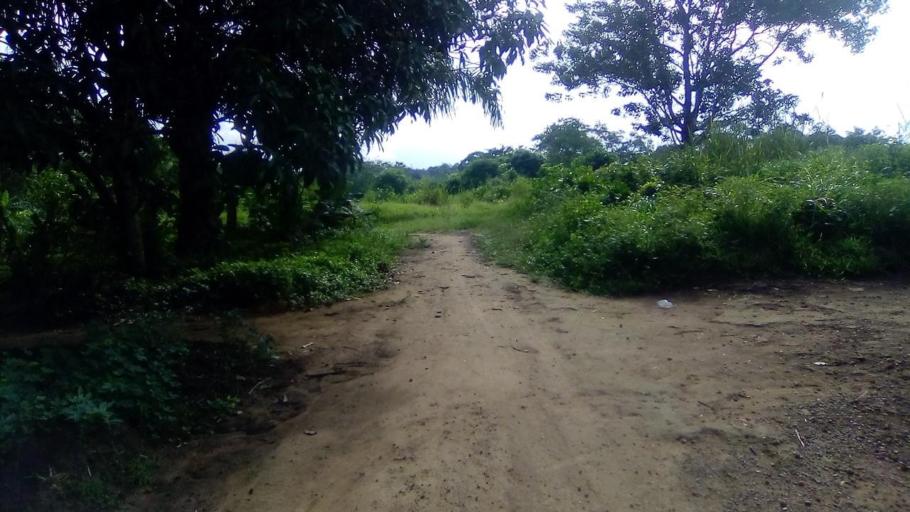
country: SL
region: Southern Province
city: Pujehun
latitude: 7.3648
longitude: -11.7210
